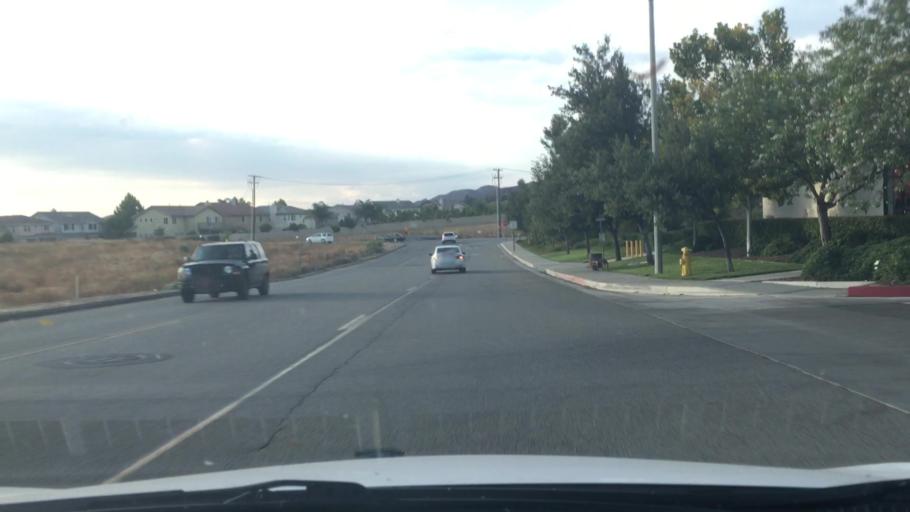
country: US
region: California
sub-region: Riverside County
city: Wildomar
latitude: 33.5966
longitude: -117.2483
